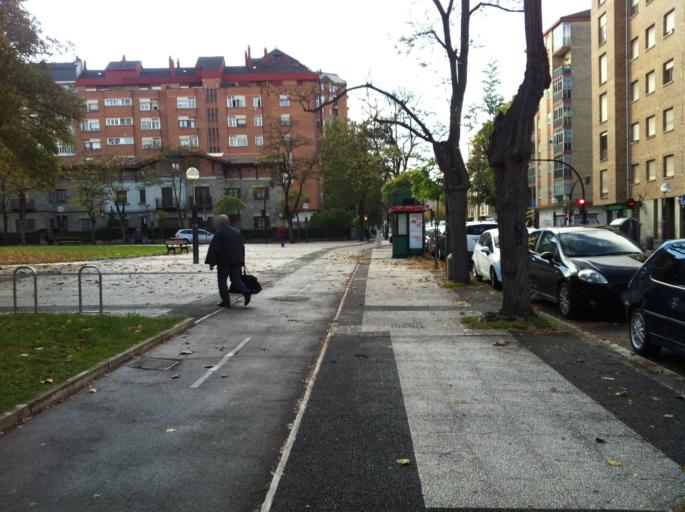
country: ES
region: Basque Country
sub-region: Provincia de Alava
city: Gasteiz / Vitoria
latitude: 42.8368
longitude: -2.6692
